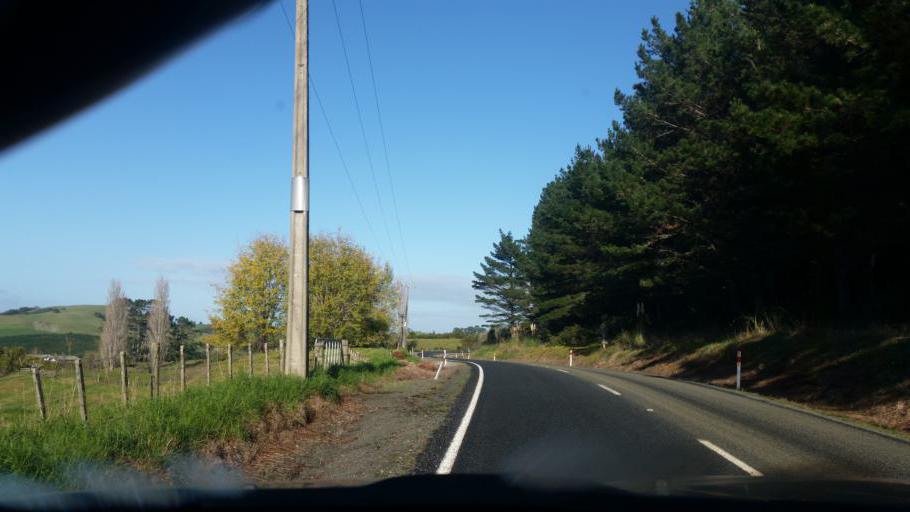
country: NZ
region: Auckland
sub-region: Auckland
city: Wellsford
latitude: -36.2286
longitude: 174.4466
